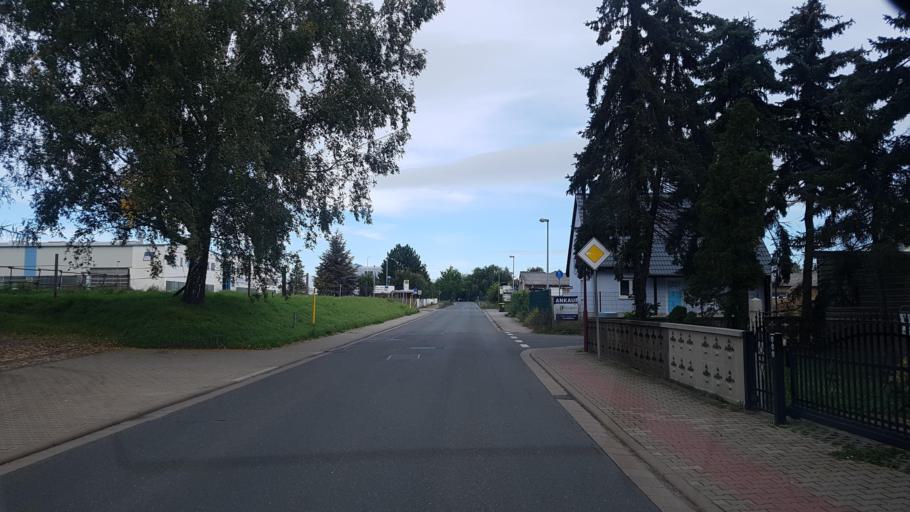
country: DE
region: Saxony
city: Pegau
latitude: 51.1737
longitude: 12.2499
